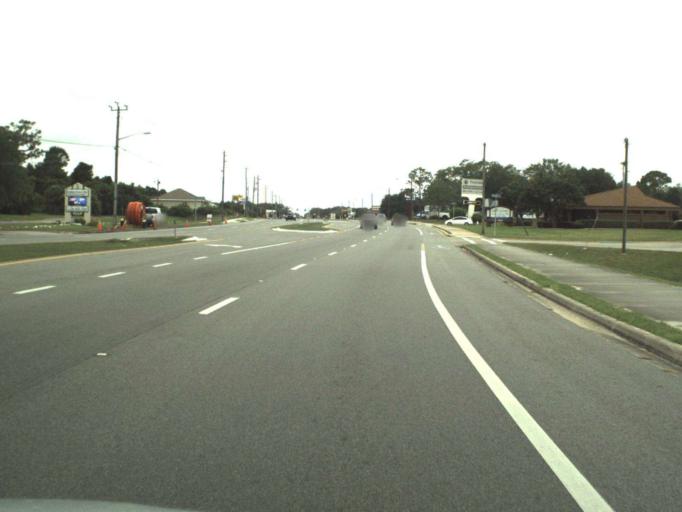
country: US
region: Florida
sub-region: Brevard County
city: Titusville
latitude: 28.5576
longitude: -80.8170
